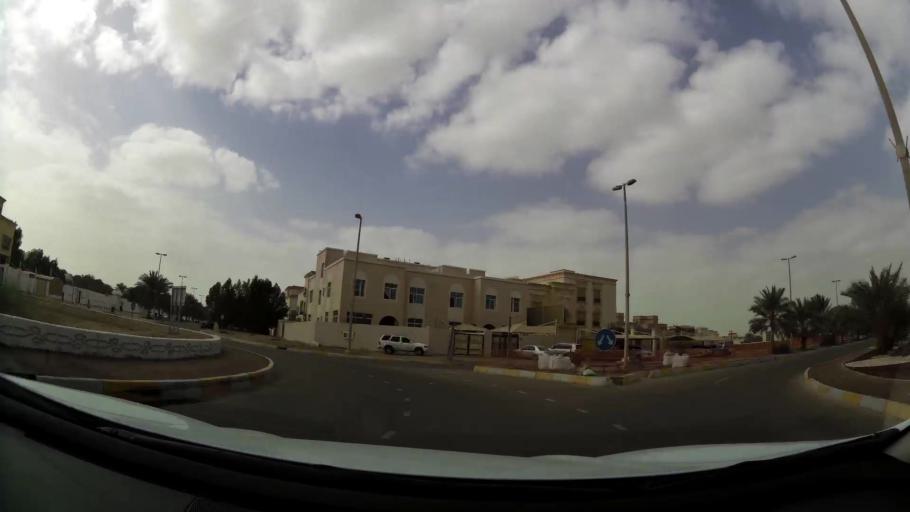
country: AE
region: Abu Dhabi
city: Abu Dhabi
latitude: 24.4106
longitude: 54.4965
